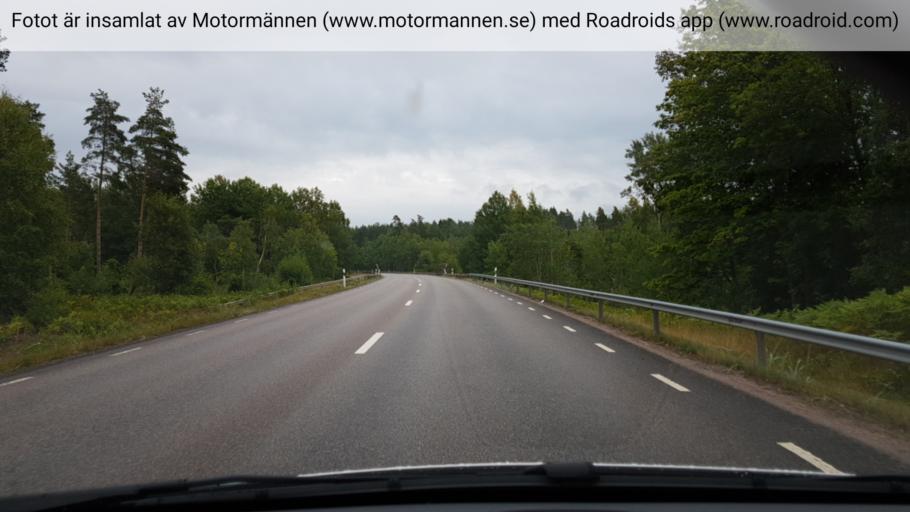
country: SE
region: Vaestra Goetaland
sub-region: Tibro Kommun
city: Tibro
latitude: 58.4540
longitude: 14.2535
